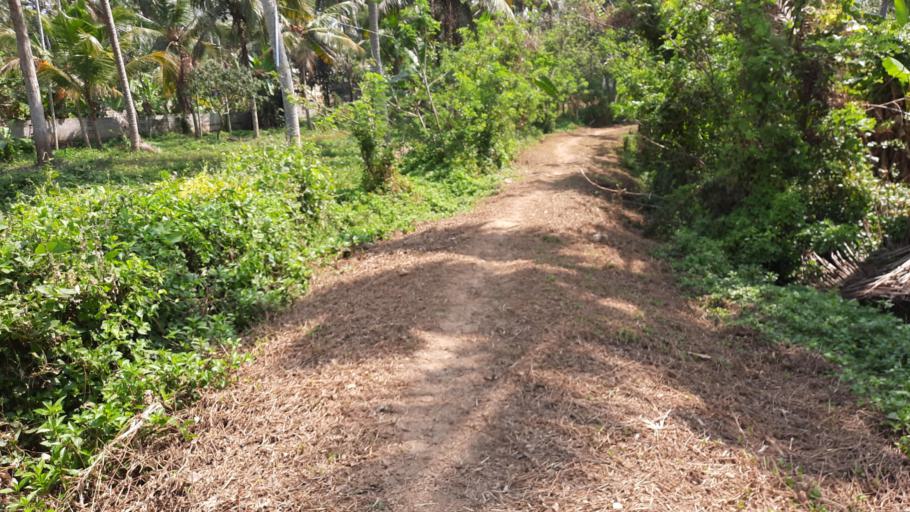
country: IN
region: Kerala
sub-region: Thiruvananthapuram
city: Thiruvananthapuram
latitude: 8.5575
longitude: 76.9329
